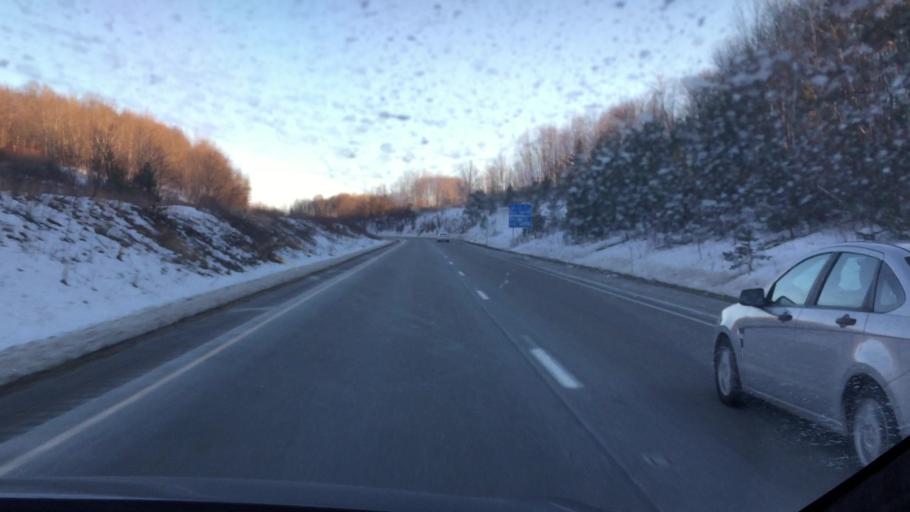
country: US
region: Pennsylvania
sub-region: Crawford County
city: Meadville
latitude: 41.6463
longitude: -80.2037
